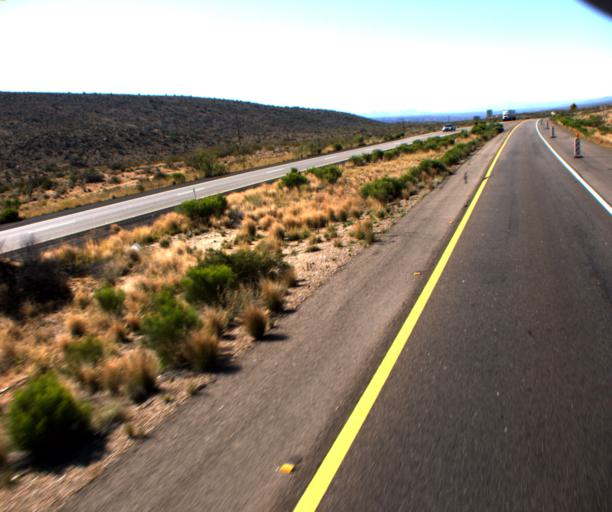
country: US
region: Arizona
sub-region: Mohave County
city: Kingman
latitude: 34.9502
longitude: -113.6681
